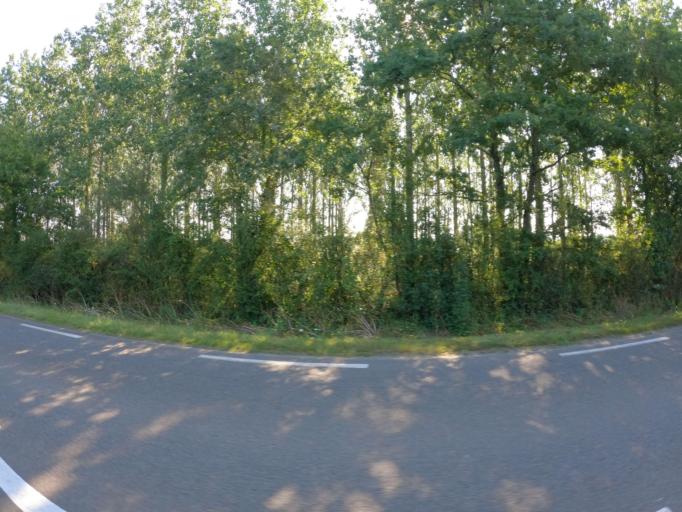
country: FR
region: Pays de la Loire
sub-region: Departement de la Loire-Atlantique
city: Pont-Saint-Martin
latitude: 47.1024
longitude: -1.5508
